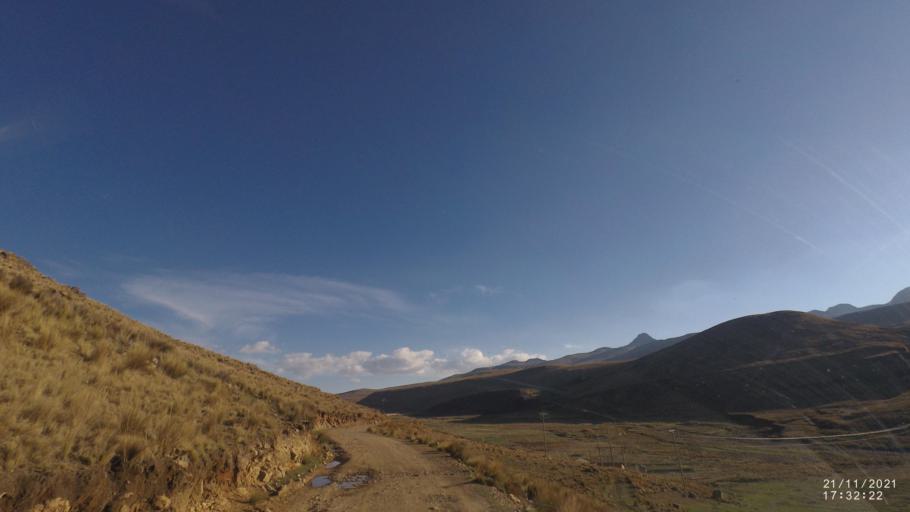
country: BO
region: Cochabamba
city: Cochabamba
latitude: -17.1898
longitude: -66.2476
